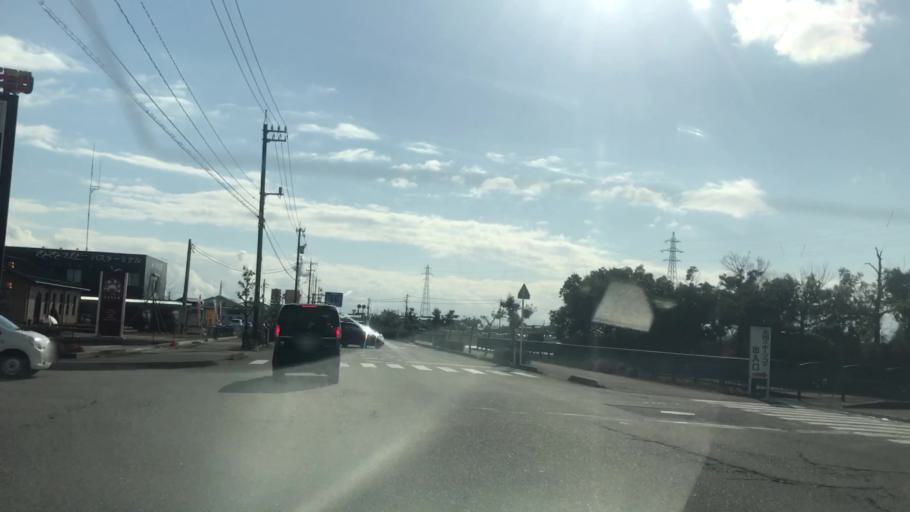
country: JP
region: Toyama
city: Takaoka
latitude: 36.7207
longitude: 137.0134
